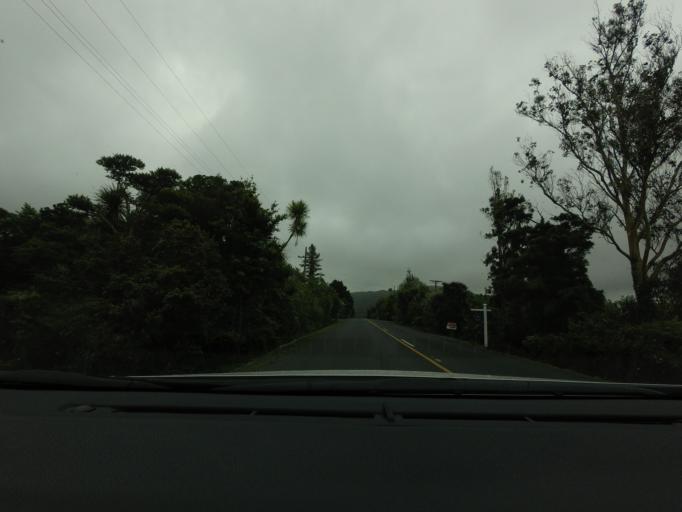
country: NZ
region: Auckland
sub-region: Auckland
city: Warkworth
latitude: -36.2829
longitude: 174.6428
